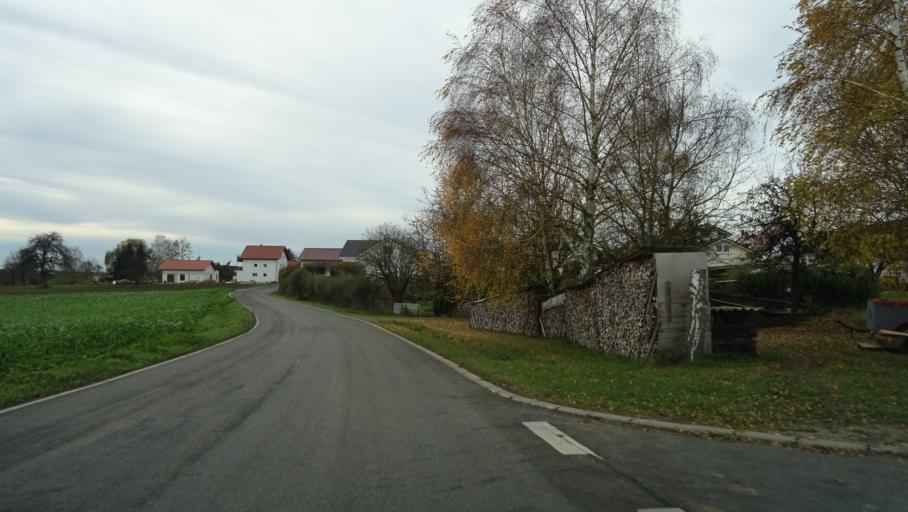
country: DE
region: Baden-Wuerttemberg
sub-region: Karlsruhe Region
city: Neckargerach
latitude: 49.3957
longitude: 9.1022
